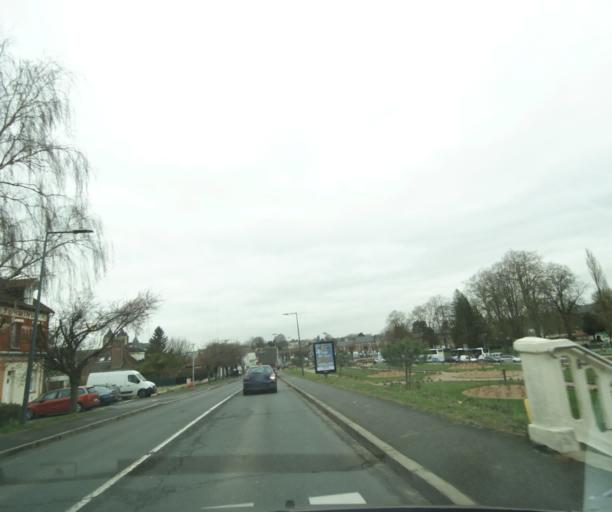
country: FR
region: Picardie
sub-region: Departement de l'Oise
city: Noyon
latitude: 49.5771
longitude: 3.0054
